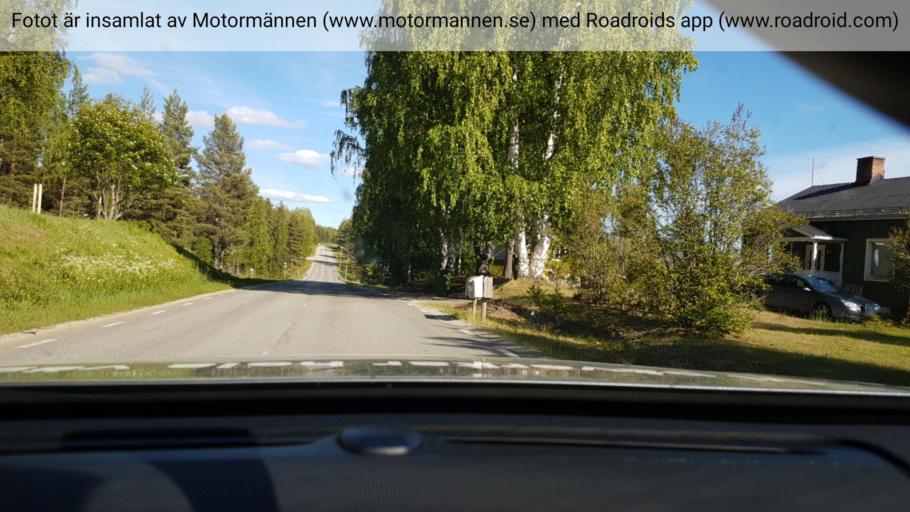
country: SE
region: Vaesterbotten
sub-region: Lycksele Kommun
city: Lycksele
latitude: 64.8104
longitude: 18.9222
